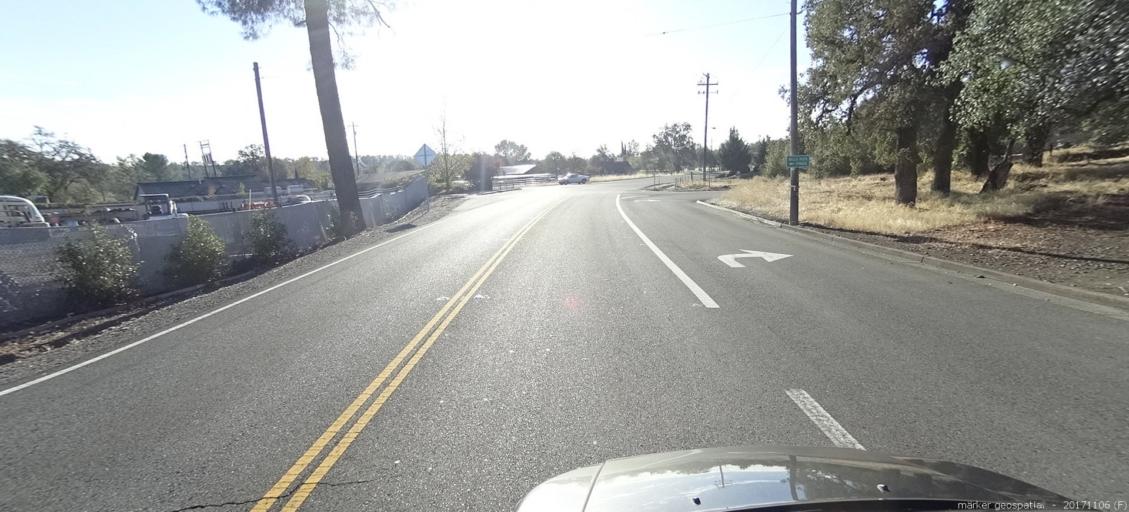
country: US
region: California
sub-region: Shasta County
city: Bella Vista
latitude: 40.6372
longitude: -122.2410
